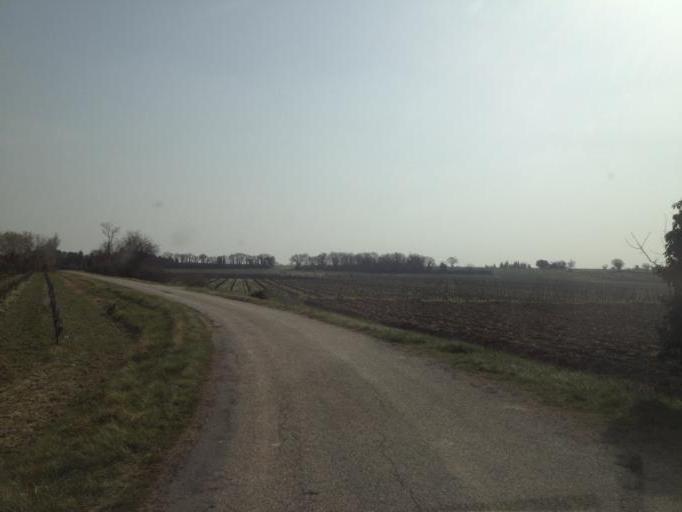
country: FR
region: Provence-Alpes-Cote d'Azur
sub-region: Departement du Vaucluse
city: Jonquieres
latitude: 44.0861
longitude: 4.9180
